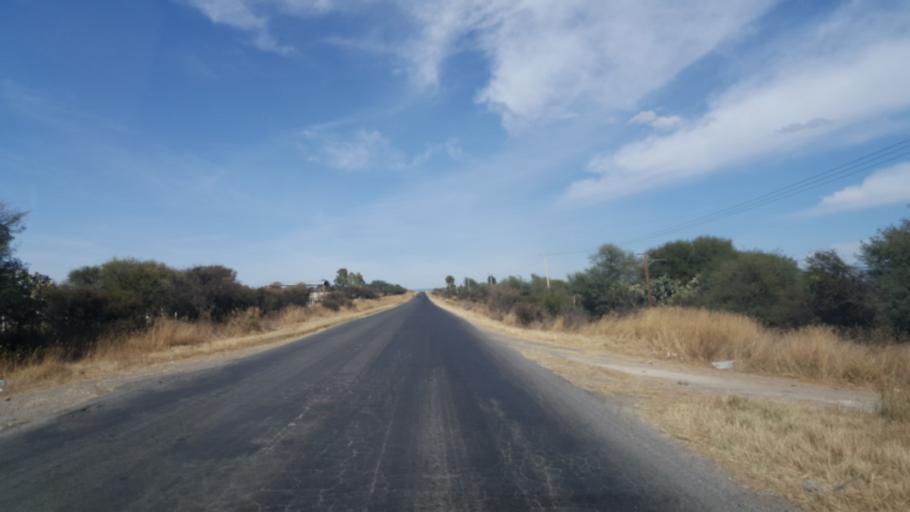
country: MX
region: Jalisco
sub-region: Lagos de Moreno
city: Geovillas Laureles del Campanario
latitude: 21.2972
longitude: -101.9287
